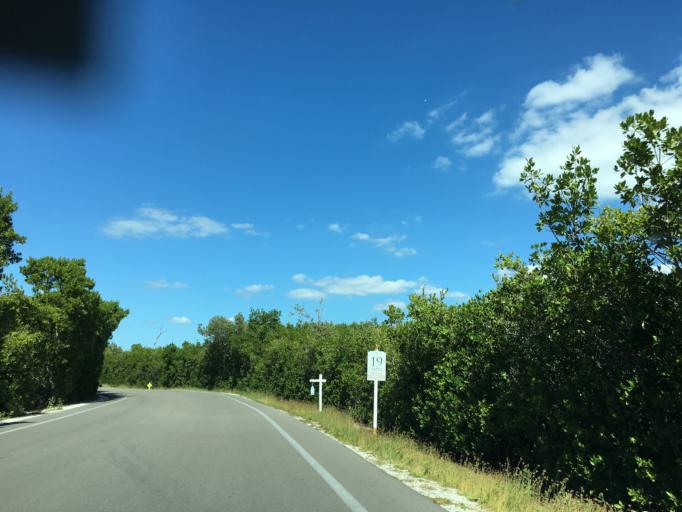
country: US
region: Florida
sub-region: Lee County
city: Pine Island Center
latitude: 26.5383
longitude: -82.1943
